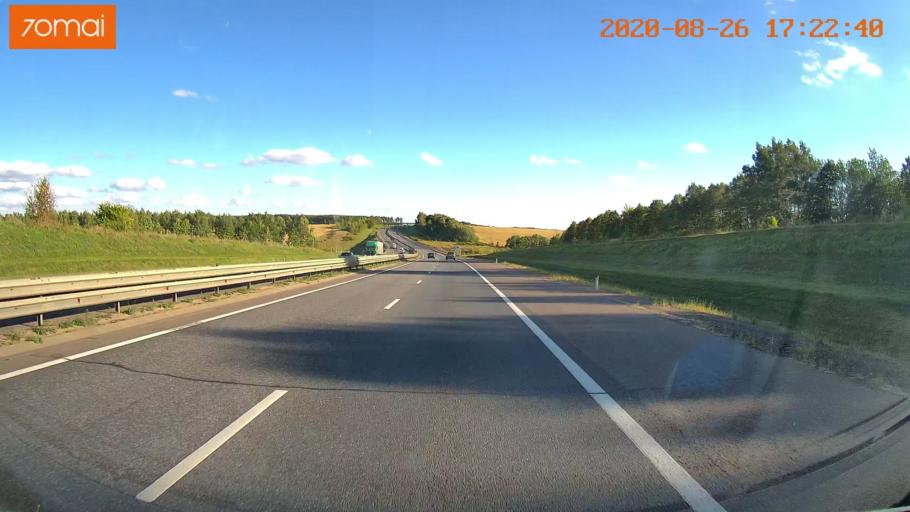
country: RU
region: Tula
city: Volovo
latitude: 53.5464
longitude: 38.1133
